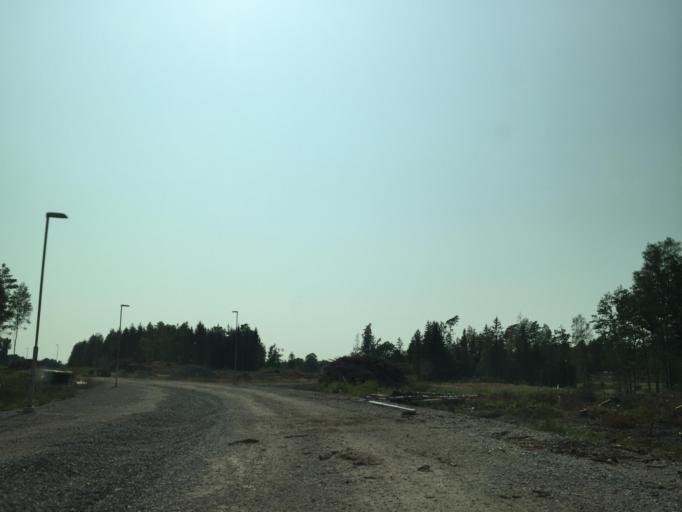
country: SE
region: Vaestra Goetaland
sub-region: Vanersborgs Kommun
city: Vanersborg
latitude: 58.3641
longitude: 12.2885
